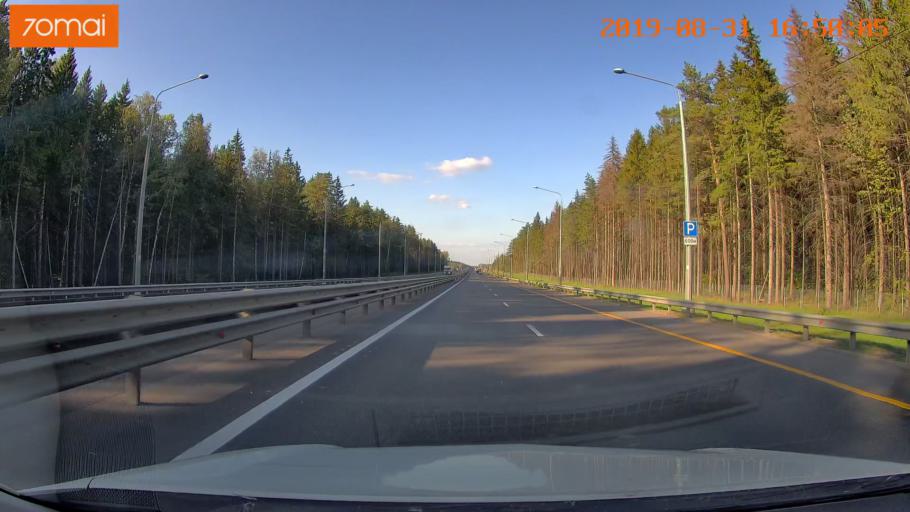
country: RU
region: Kaluga
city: Pyatovskiy
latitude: 54.7020
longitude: 36.1597
